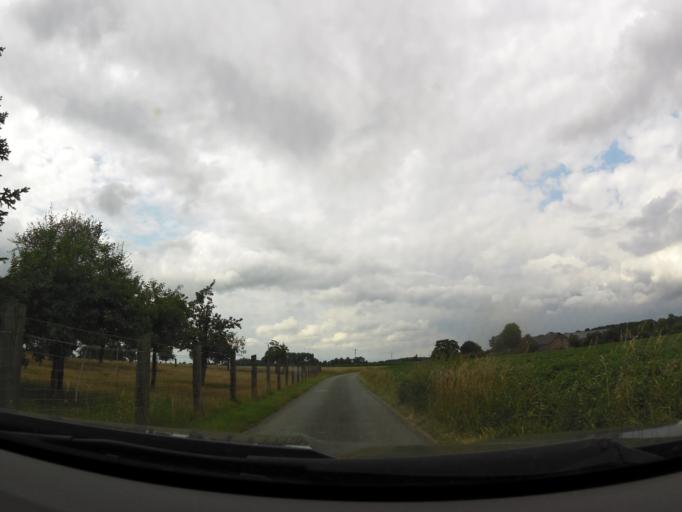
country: DE
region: North Rhine-Westphalia
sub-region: Regierungsbezirk Dusseldorf
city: Sonsbeck
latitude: 51.5826
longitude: 6.3344
